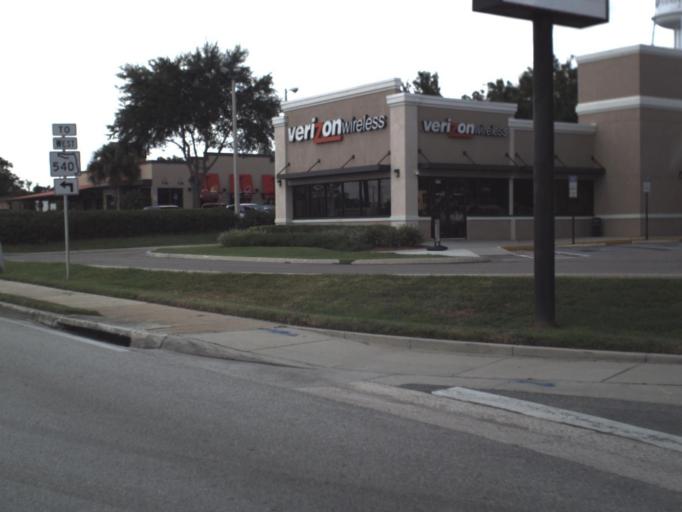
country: US
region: Florida
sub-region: Polk County
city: Winter Haven
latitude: 28.0041
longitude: -81.7287
